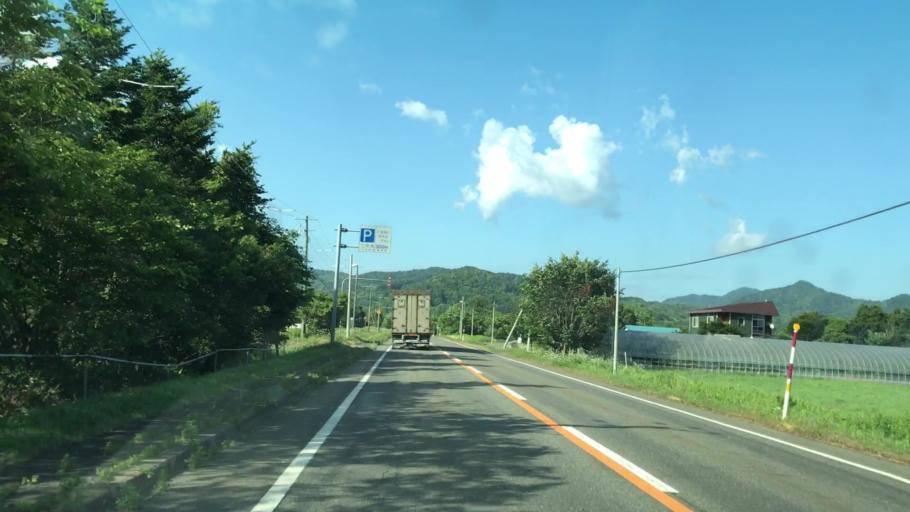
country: JP
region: Hokkaido
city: Shimo-furano
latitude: 42.8724
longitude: 142.4282
